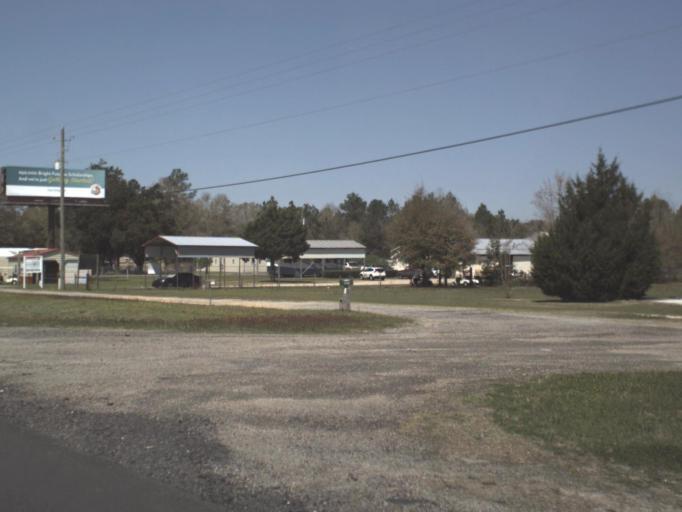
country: US
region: Florida
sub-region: Walton County
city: DeFuniak Springs
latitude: 30.7350
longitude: -86.1537
